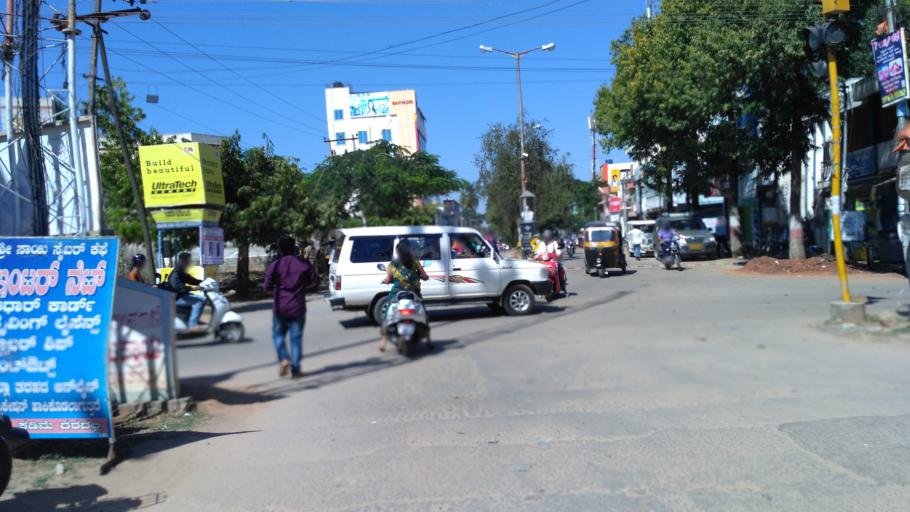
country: IN
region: Karnataka
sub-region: Hassan
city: Hassan
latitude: 13.0108
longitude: 76.1060
